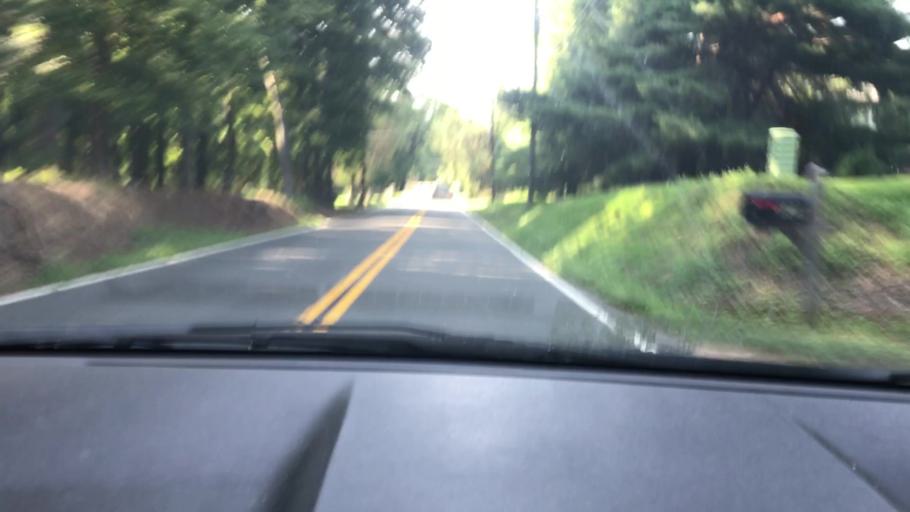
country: US
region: Virginia
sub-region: Fairfax County
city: Great Falls
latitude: 38.9932
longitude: -77.2610
